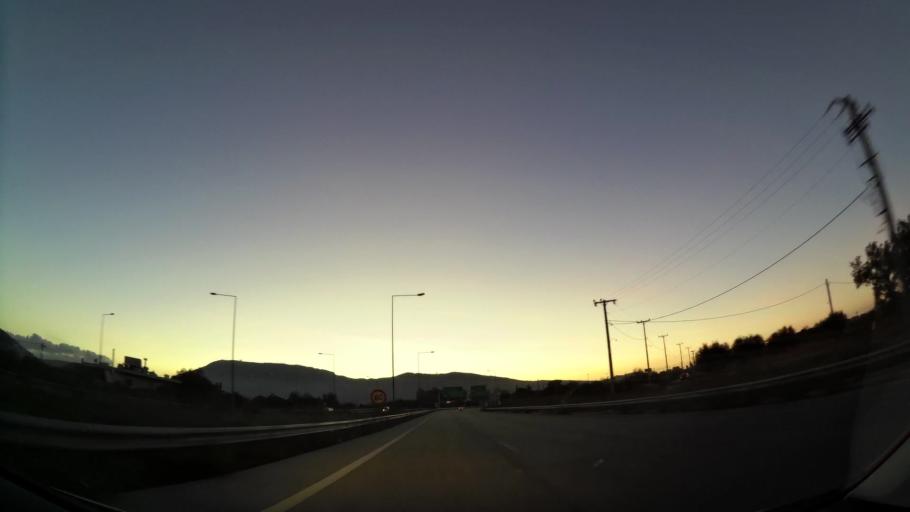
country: GR
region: Attica
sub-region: Nomarchia Anatolikis Attikis
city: Argithea
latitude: 37.9926
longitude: 23.8959
